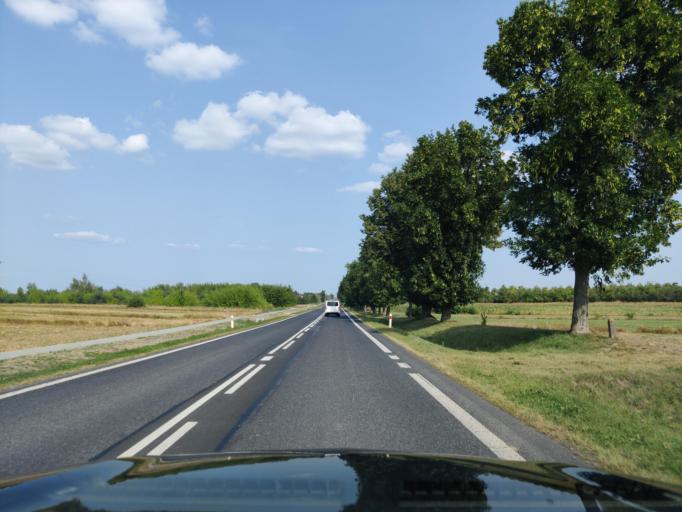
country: PL
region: Masovian Voivodeship
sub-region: Powiat makowski
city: Rozan
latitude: 52.8789
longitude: 21.3671
